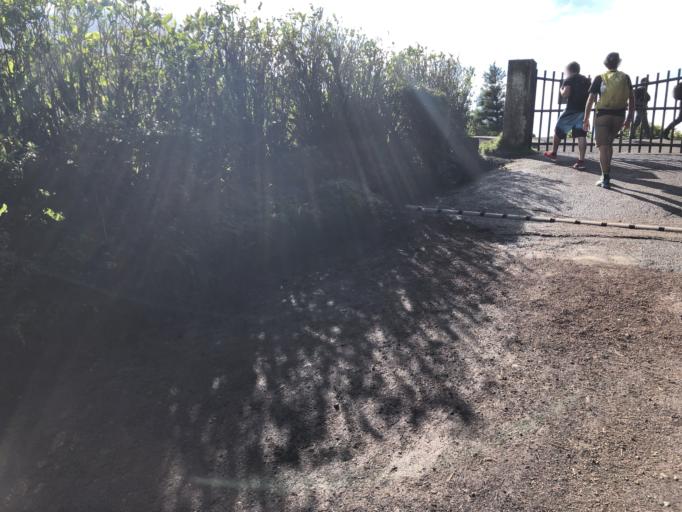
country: PT
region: Azores
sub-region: Ponta Delgada
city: Arrifes
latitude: 37.8352
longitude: -25.7586
